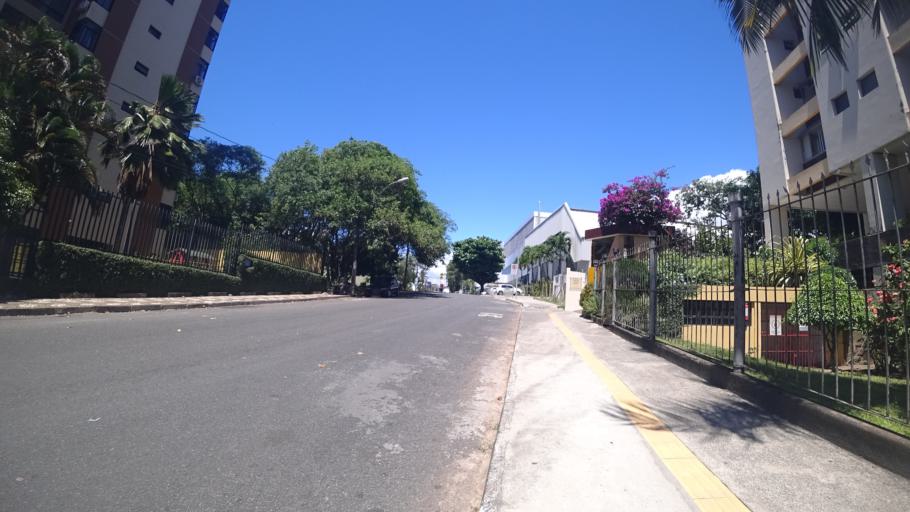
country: BR
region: Bahia
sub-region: Salvador
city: Salvador
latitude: -12.9910
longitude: -38.4619
